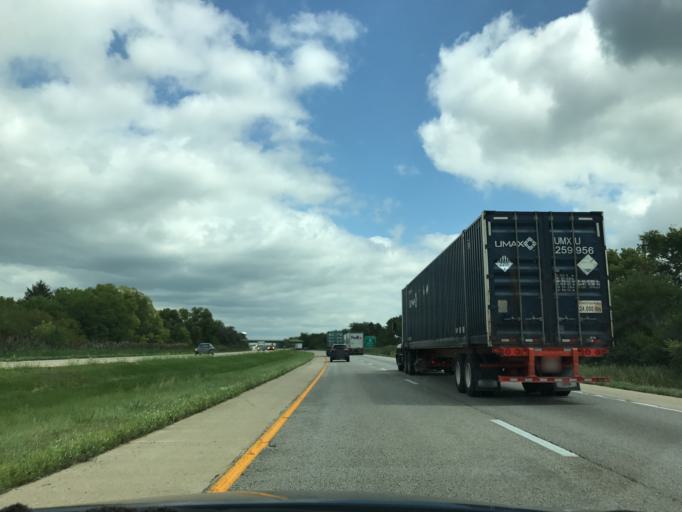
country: US
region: Illinois
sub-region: Grundy County
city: Morris
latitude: 41.3801
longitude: -88.4381
